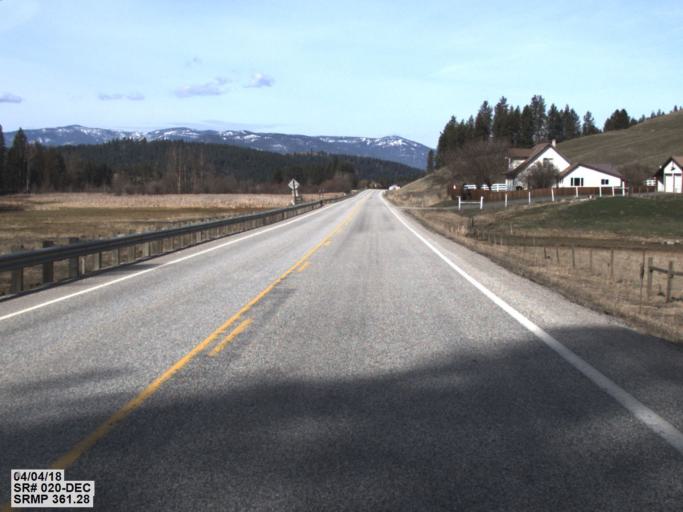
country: US
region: Washington
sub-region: Stevens County
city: Colville
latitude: 48.5149
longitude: -117.7821
